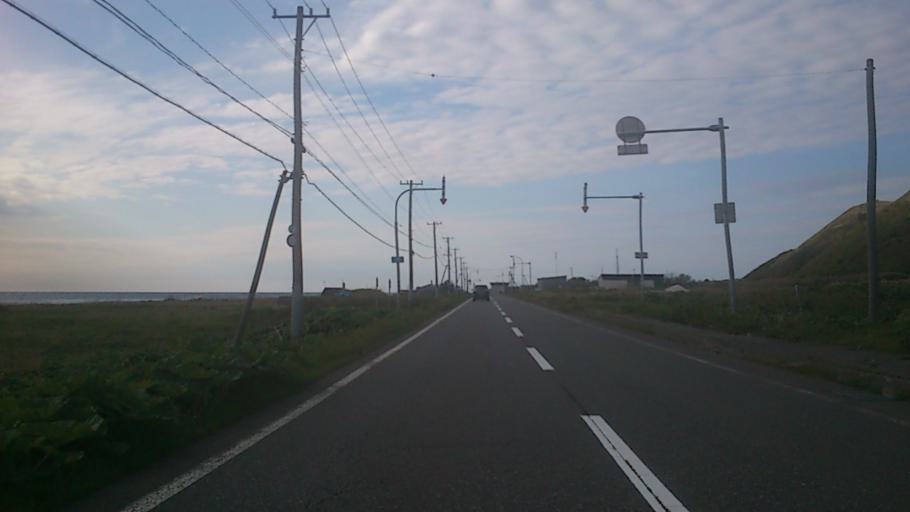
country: JP
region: Hokkaido
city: Wakkanai
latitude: 45.4011
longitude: 141.6369
